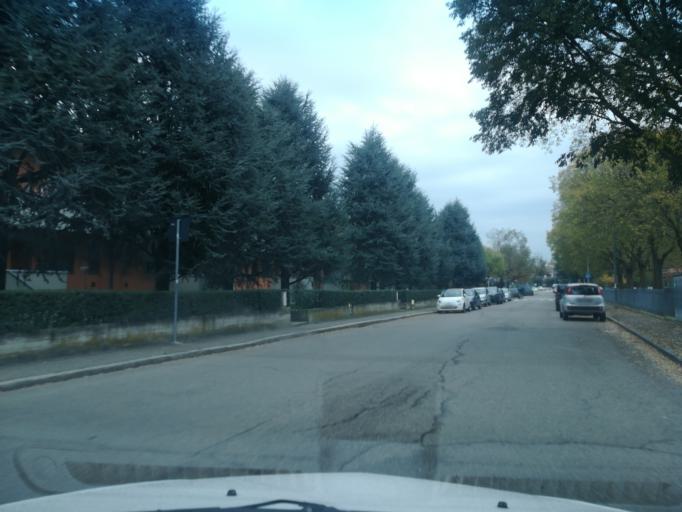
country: IT
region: Emilia-Romagna
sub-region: Provincia di Bologna
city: Imola
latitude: 44.3655
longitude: 11.6893
